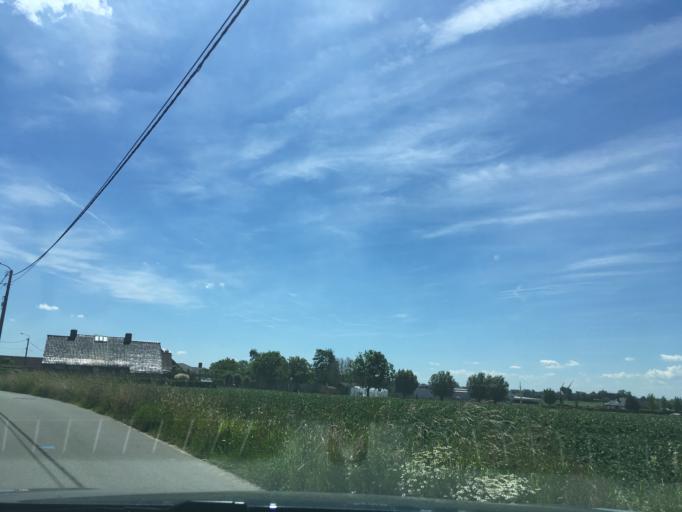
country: BE
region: Flanders
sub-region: Provincie West-Vlaanderen
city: Hooglede
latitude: 51.0058
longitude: 3.0929
